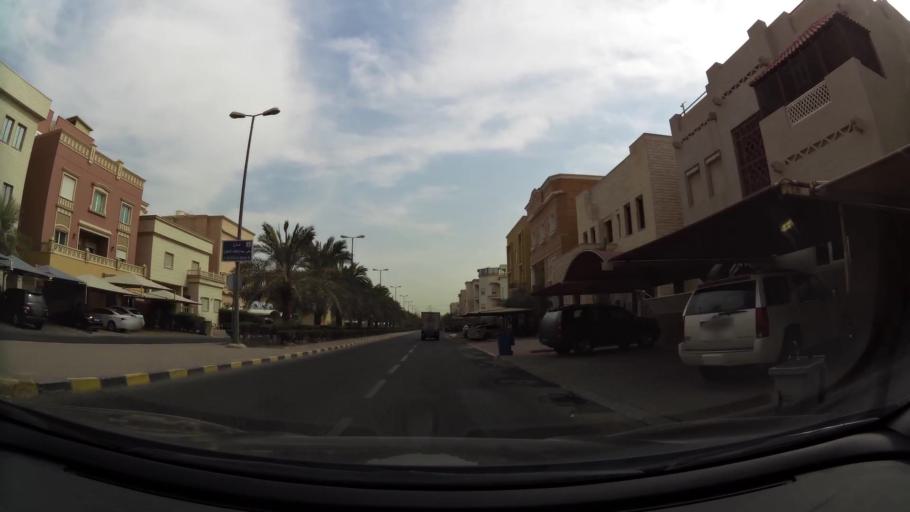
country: KW
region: Mubarak al Kabir
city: Sabah as Salim
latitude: 29.2712
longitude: 48.0295
